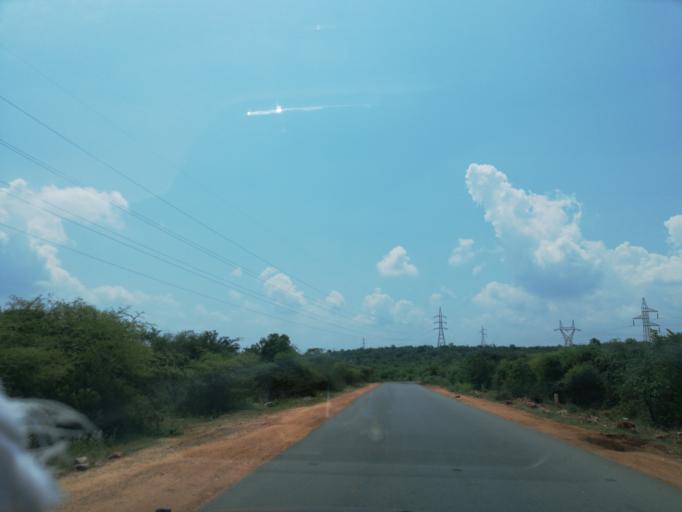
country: IN
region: Andhra Pradesh
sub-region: Guntur
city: Macherla
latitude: 16.5661
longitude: 79.3478
